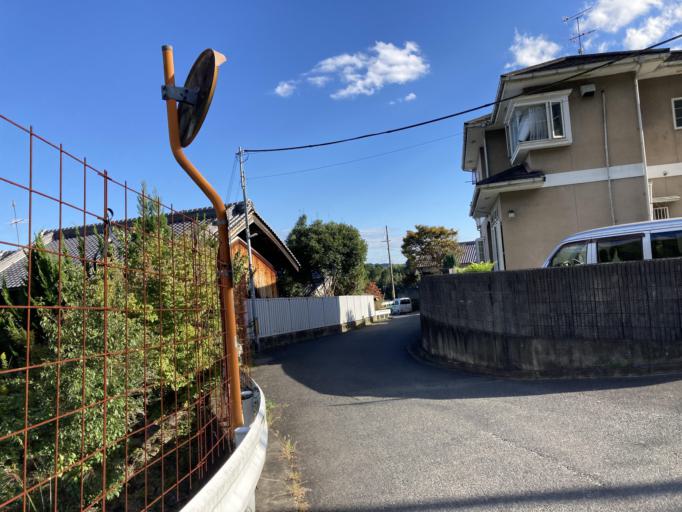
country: JP
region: Nara
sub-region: Ikoma-shi
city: Ikoma
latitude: 34.6703
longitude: 135.6934
